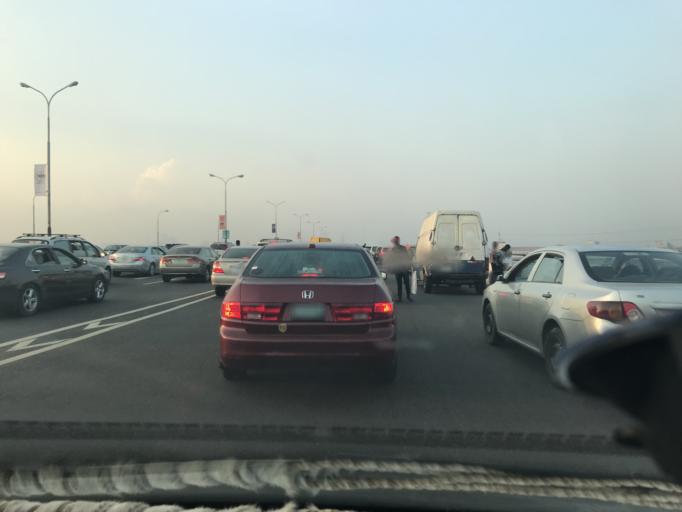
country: NG
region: Lagos
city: Ebute Metta
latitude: 6.4838
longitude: 3.3934
